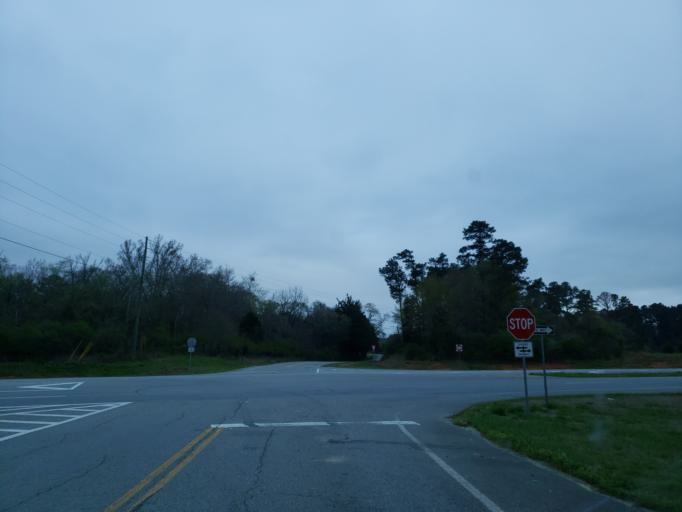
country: US
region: Georgia
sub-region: Bartow County
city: Euharlee
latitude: 34.0844
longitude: -84.9793
